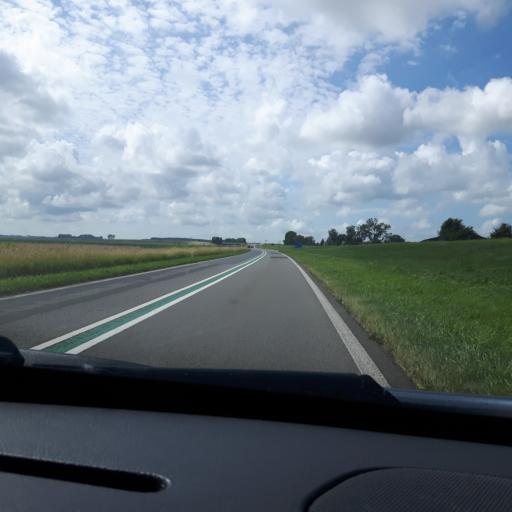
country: NL
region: Zeeland
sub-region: Gemeente Goes
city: Goes
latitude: 51.5771
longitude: 3.8190
